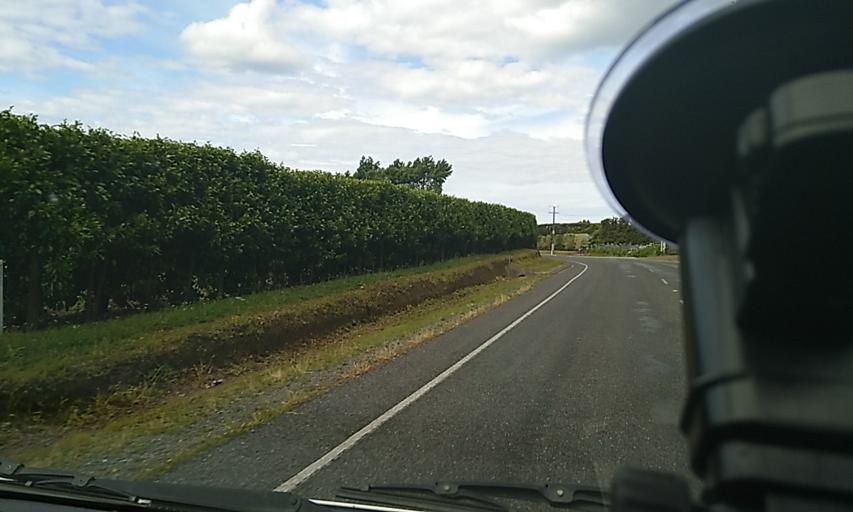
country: NZ
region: Bay of Plenty
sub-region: Western Bay of Plenty District
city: Waihi Beach
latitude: -37.4490
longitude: 175.9523
